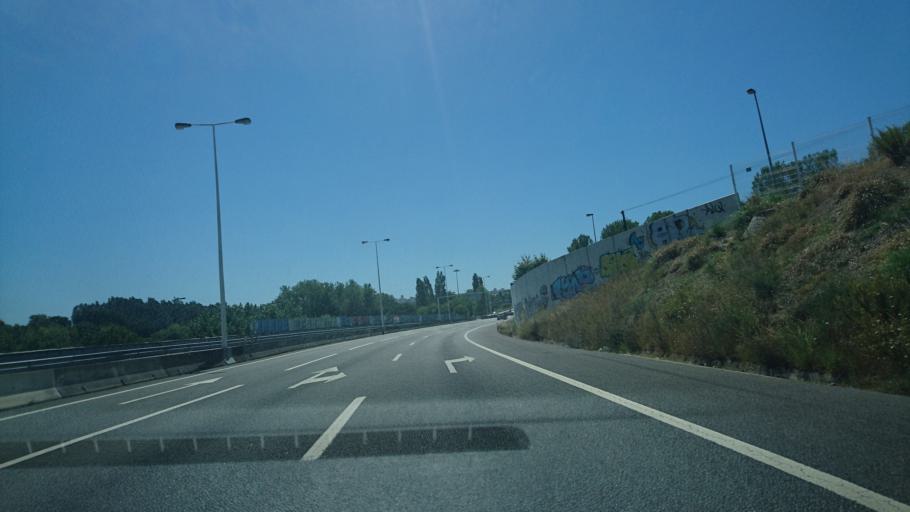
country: PT
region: Porto
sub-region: Gondomar
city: Valbom
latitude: 41.1533
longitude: -8.5733
